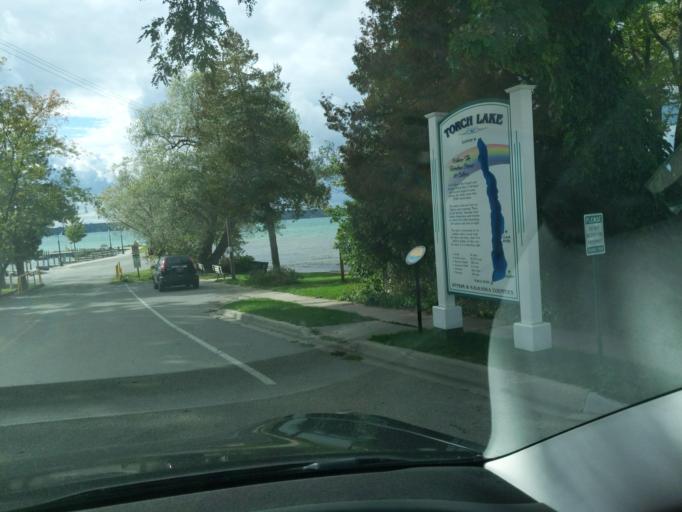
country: US
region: Michigan
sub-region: Kalkaska County
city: Rapid City
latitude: 44.8813
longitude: -85.2766
